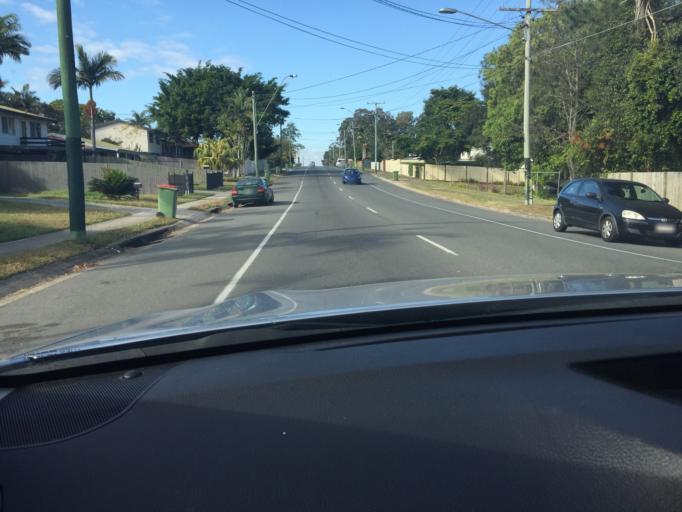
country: AU
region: Queensland
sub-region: Logan
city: Slacks Creek
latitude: -27.6408
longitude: 153.1540
